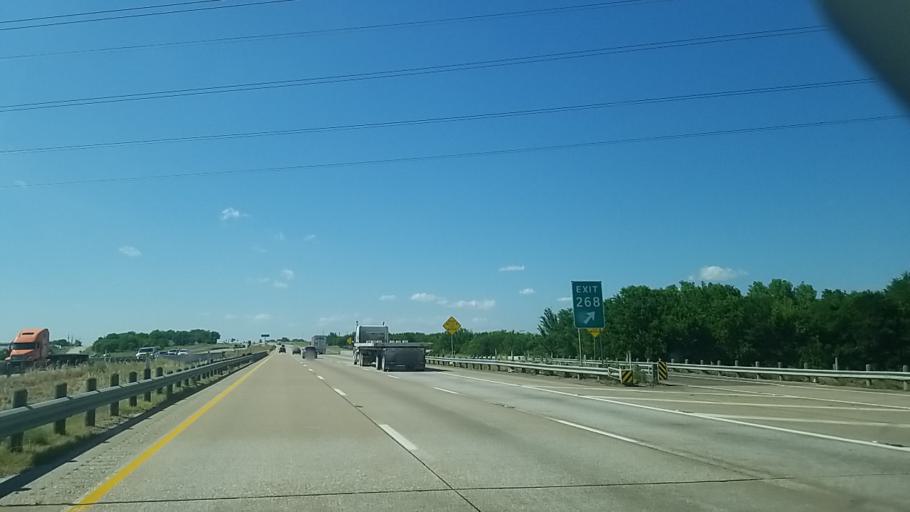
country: US
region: Texas
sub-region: Ellis County
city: Ferris
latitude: 32.5582
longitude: -96.6636
